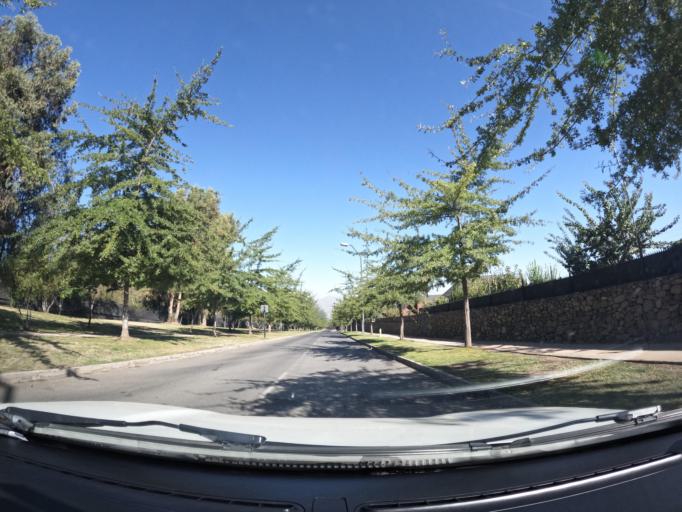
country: CL
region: Santiago Metropolitan
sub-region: Provincia de Santiago
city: Villa Presidente Frei, Nunoa, Santiago, Chile
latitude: -33.5014
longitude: -70.5202
